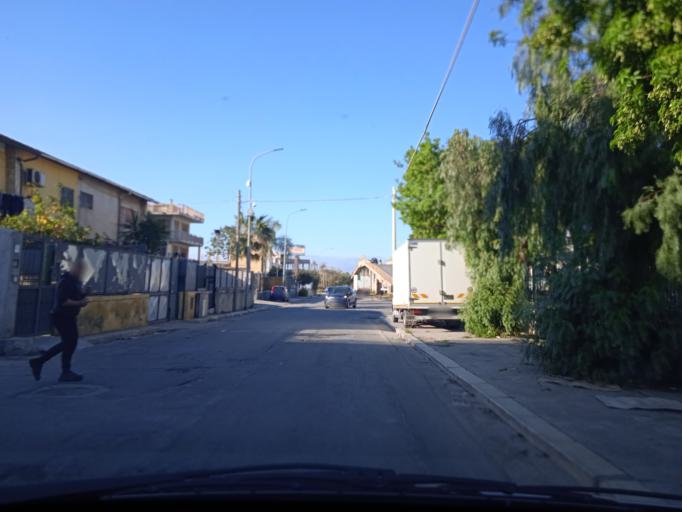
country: IT
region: Sicily
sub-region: Palermo
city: Villabate
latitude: 38.0851
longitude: 13.4497
